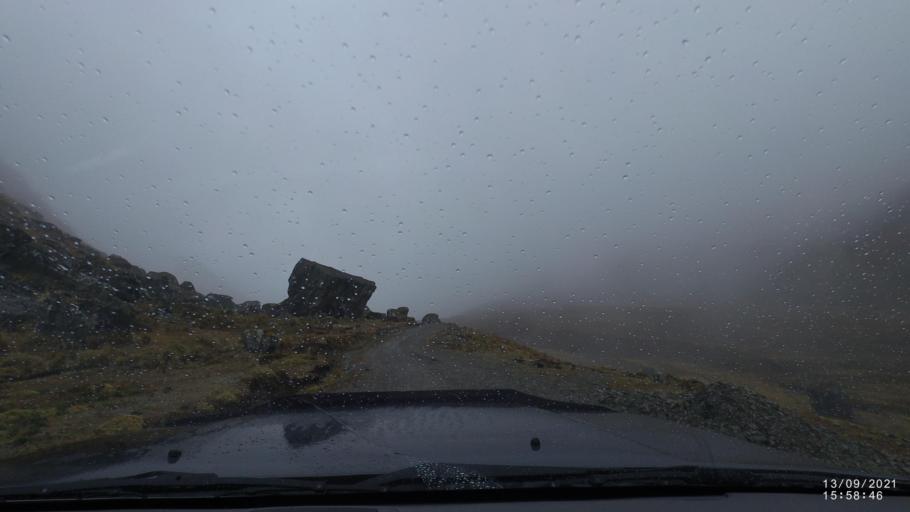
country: BO
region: Cochabamba
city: Colomi
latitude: -17.2992
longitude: -65.7056
